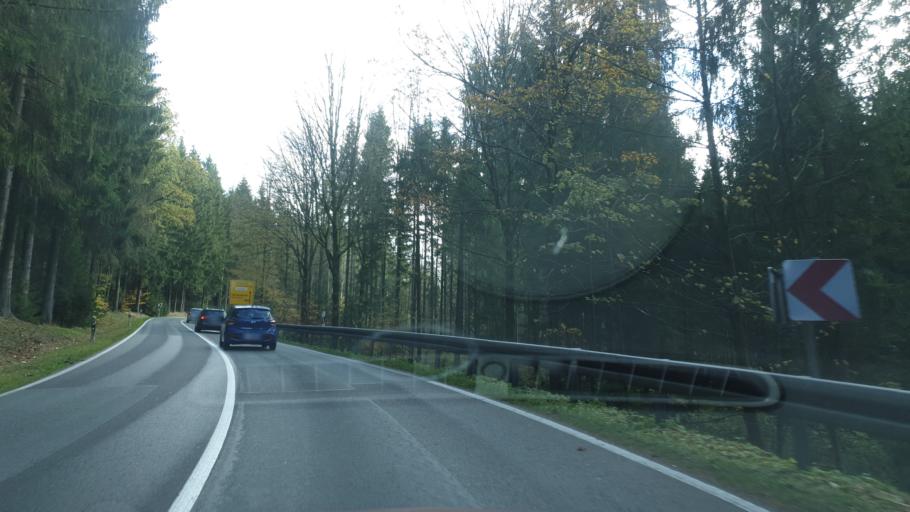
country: DE
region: Saxony
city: Eibenstock
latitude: 50.5115
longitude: 12.6085
